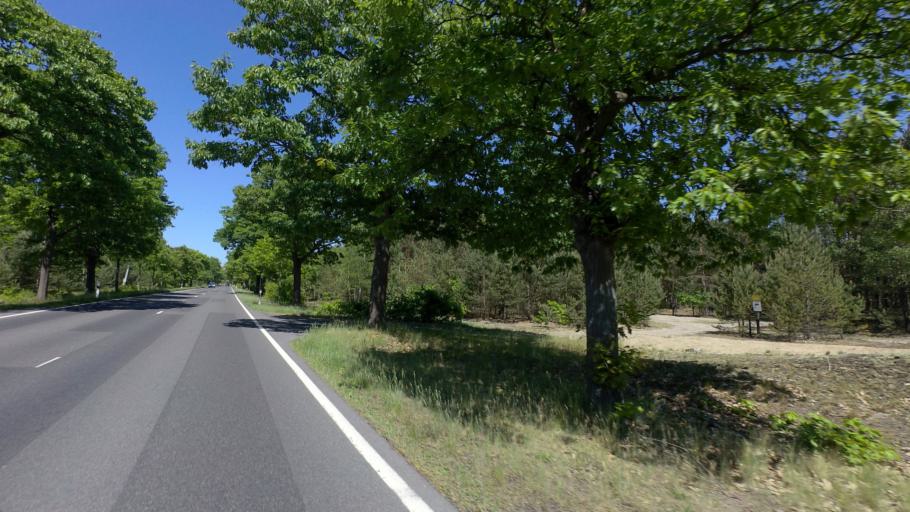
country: DE
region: Brandenburg
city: Drachhausen
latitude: 51.9293
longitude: 14.3456
